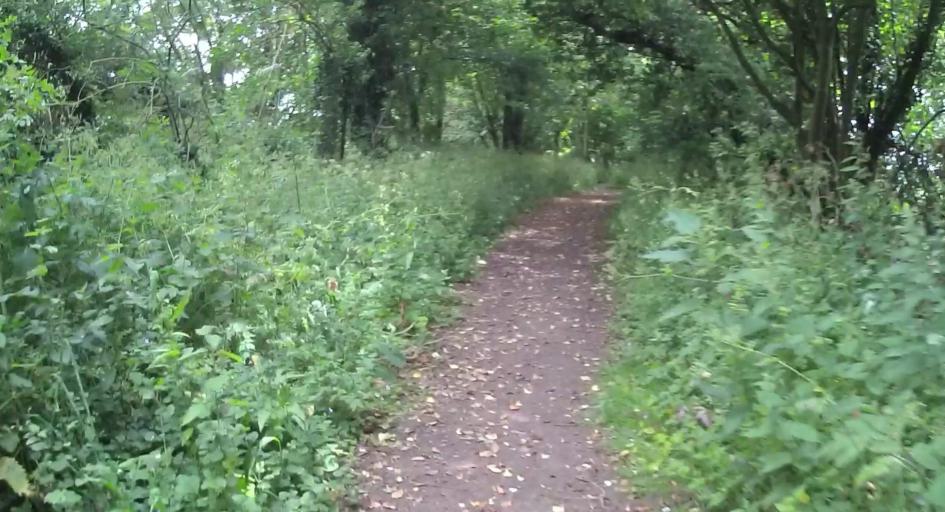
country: GB
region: England
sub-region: Hampshire
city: Basingstoke
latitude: 51.1633
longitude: -1.1631
